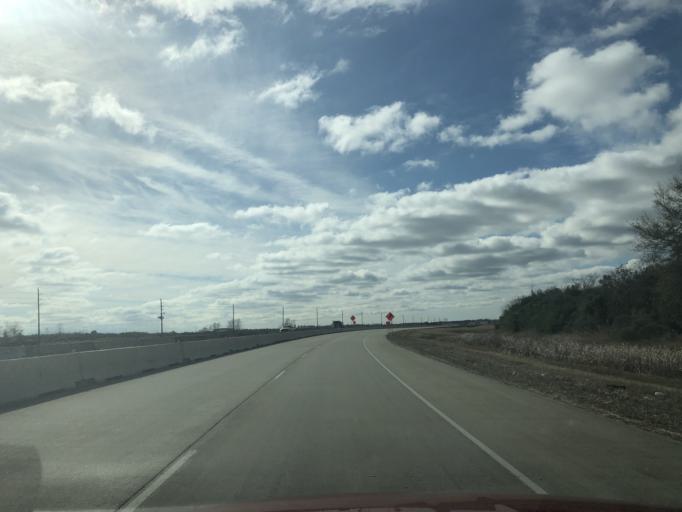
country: US
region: Texas
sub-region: Chambers County
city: Mont Belvieu
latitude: 29.8127
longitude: -94.8624
